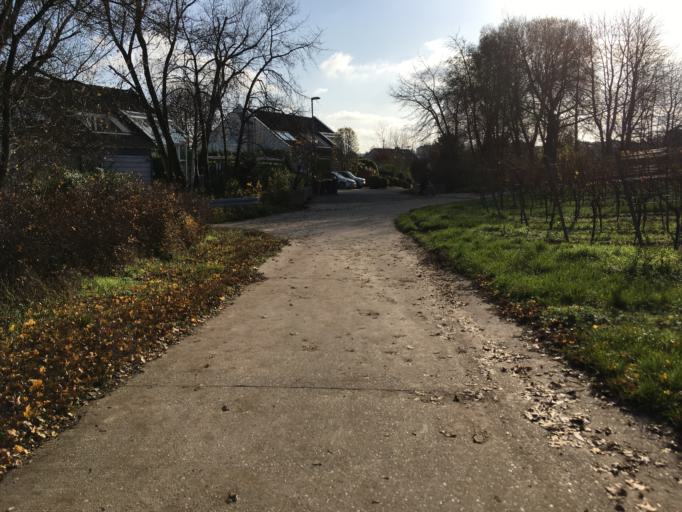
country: DE
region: Rheinland-Pfalz
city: Bodenheim
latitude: 49.9352
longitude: 8.3035
